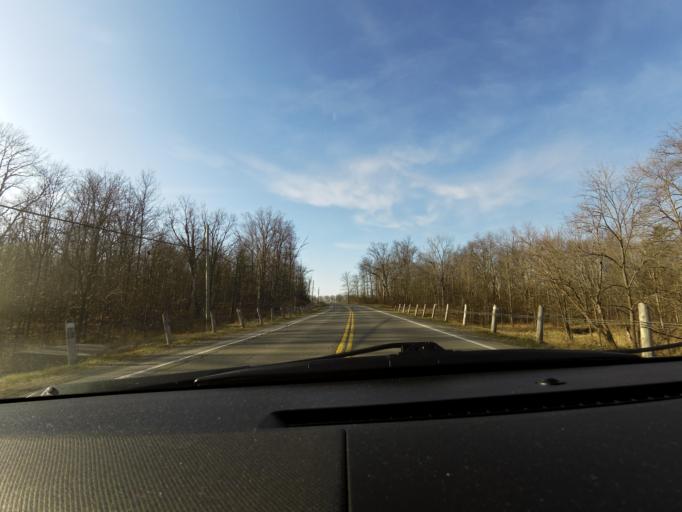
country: CA
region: Ontario
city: Ancaster
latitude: 42.9812
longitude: -79.8716
